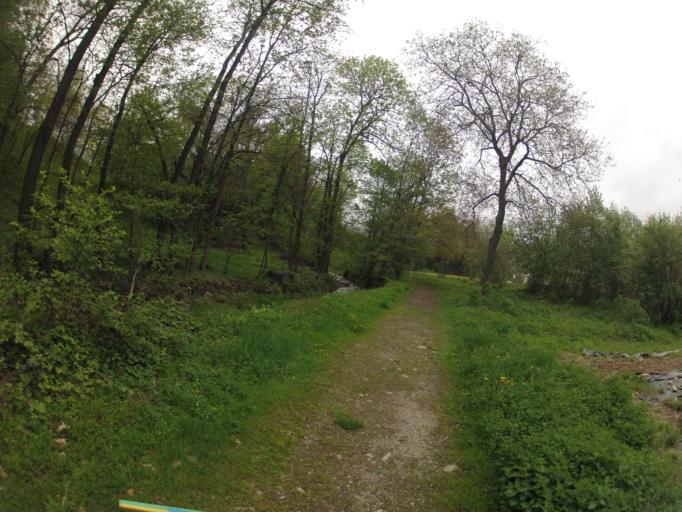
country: IT
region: Piedmont
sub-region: Provincia di Cuneo
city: Peveragno
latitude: 44.3287
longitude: 7.6101
